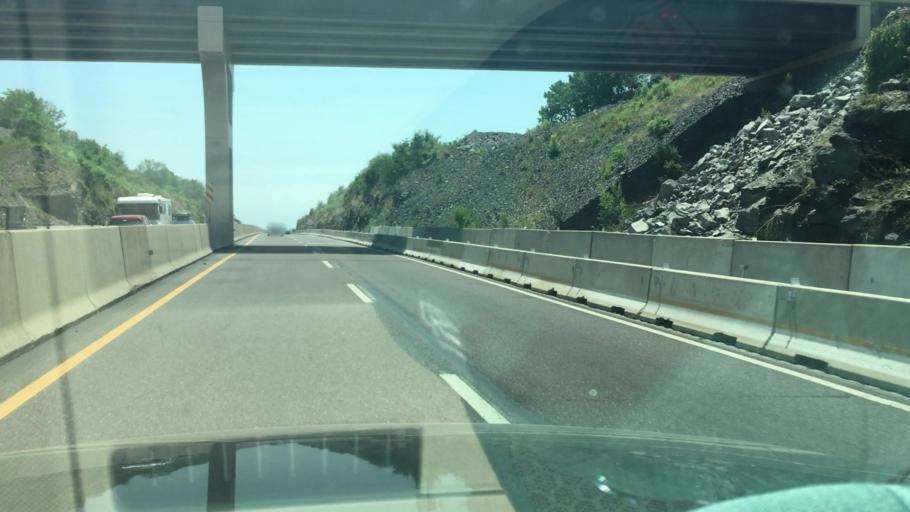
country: US
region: Pennsylvania
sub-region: Montgomery County
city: Telford
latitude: 40.3498
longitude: -75.3904
